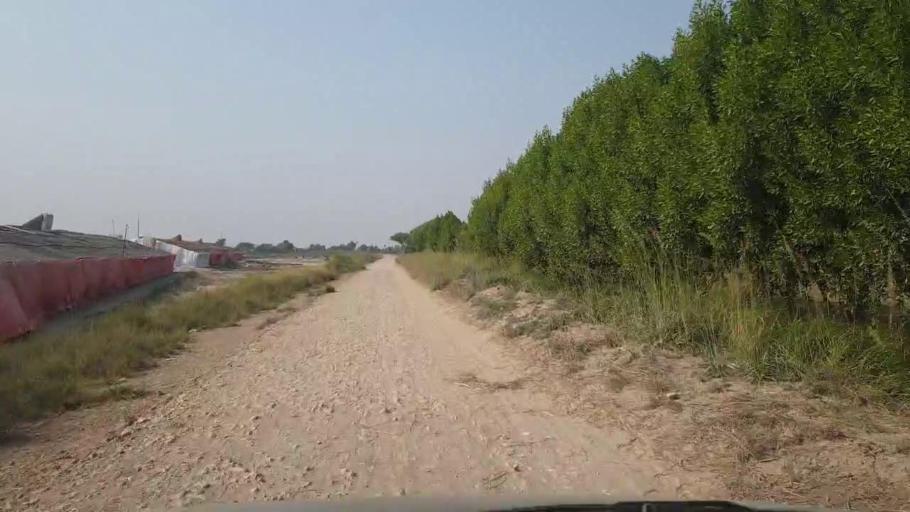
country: PK
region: Sindh
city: Tando Muhammad Khan
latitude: 25.0492
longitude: 68.3713
